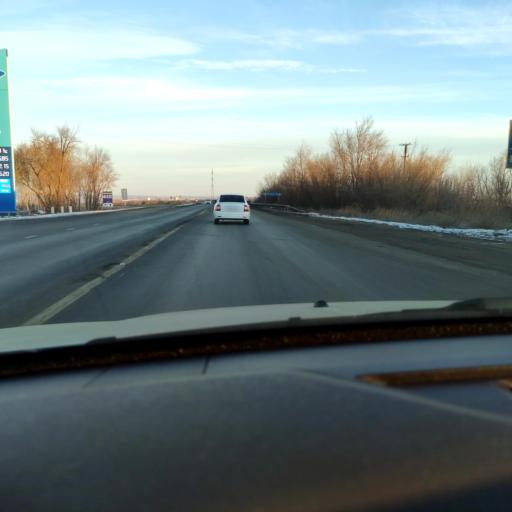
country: RU
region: Samara
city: Smyshlyayevka
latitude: 53.2556
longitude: 50.4757
